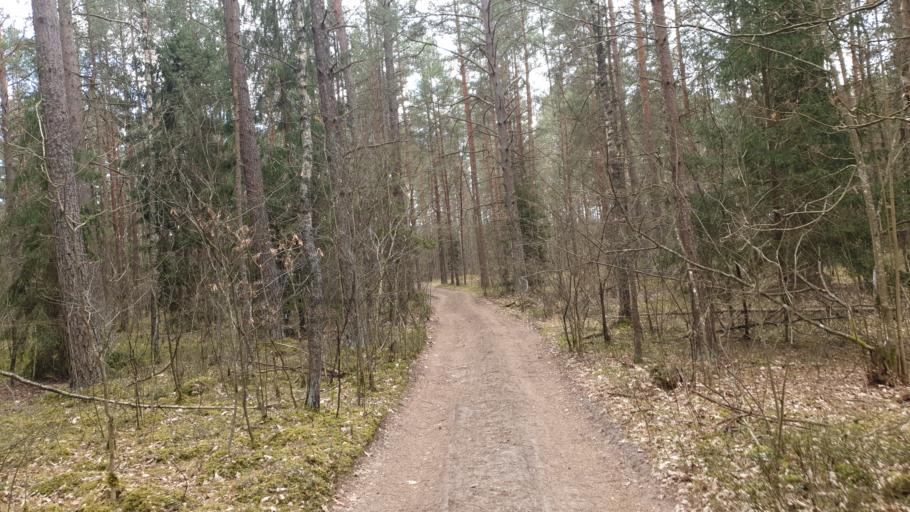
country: LT
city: Grigiskes
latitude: 54.7264
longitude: 25.0315
